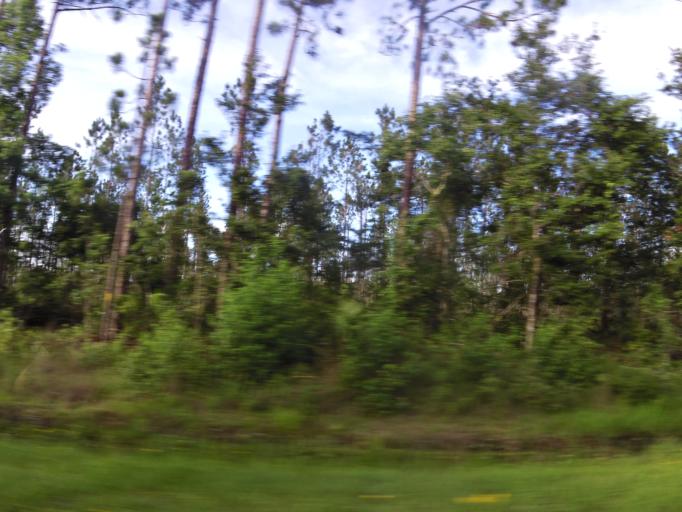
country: US
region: Florida
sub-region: Clay County
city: Green Cove Springs
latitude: 30.0007
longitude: -81.5446
